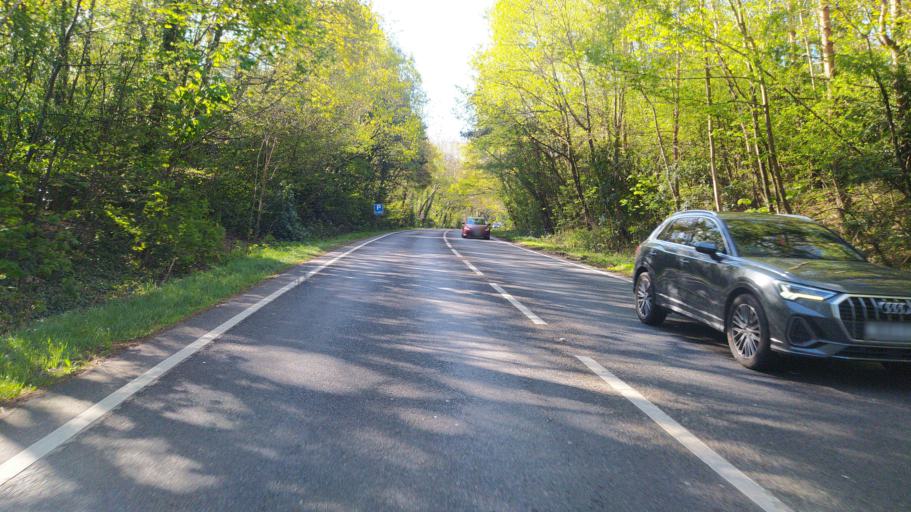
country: GB
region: England
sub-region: Hampshire
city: Marchwood
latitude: 50.8818
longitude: -1.4439
